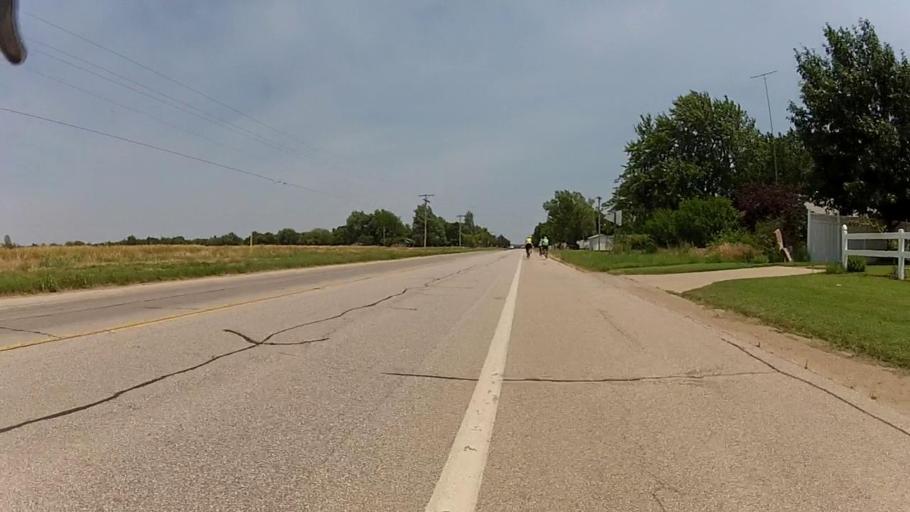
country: US
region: Kansas
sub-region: Cowley County
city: Arkansas City
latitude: 37.0565
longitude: -97.0818
